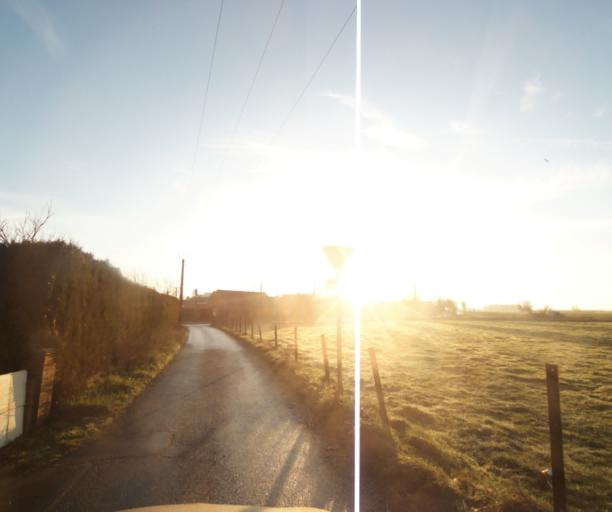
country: FR
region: Nord-Pas-de-Calais
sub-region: Departement du Nord
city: Quarouble
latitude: 50.3837
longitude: 3.6215
